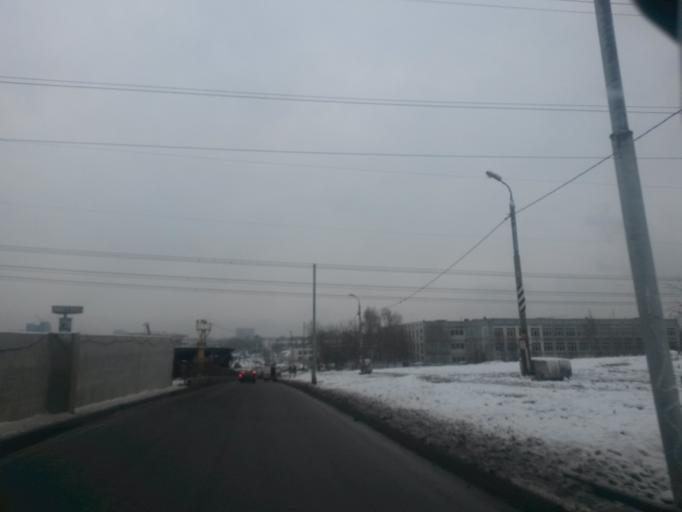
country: RU
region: Moscow
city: Mikhalkovo
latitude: 55.6892
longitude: 37.4276
